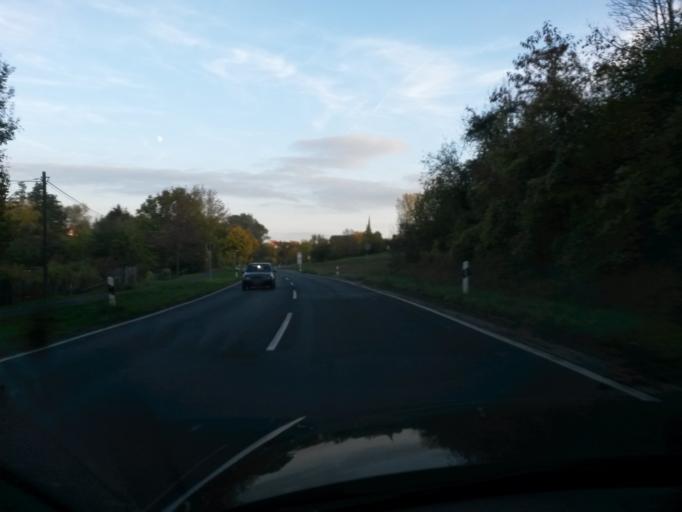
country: DE
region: Bavaria
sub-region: Regierungsbezirk Unterfranken
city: Rimpar
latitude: 49.8265
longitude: 9.9571
